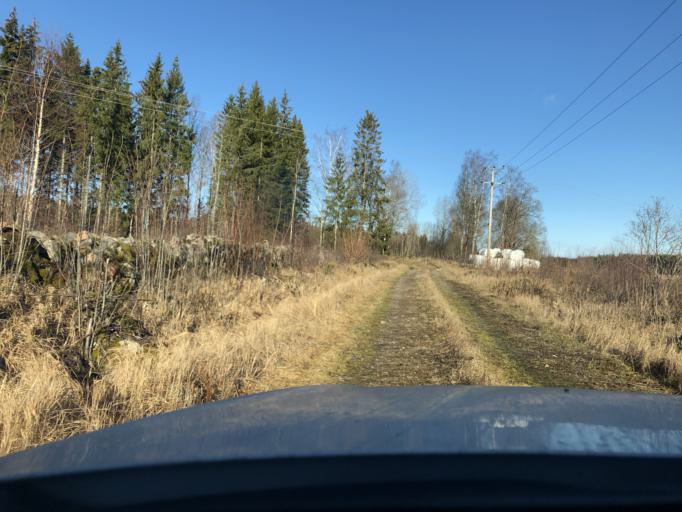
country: SE
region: Gaevleborg
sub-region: Gavle Kommun
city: Hedesunda
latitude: 60.3058
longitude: 16.9003
